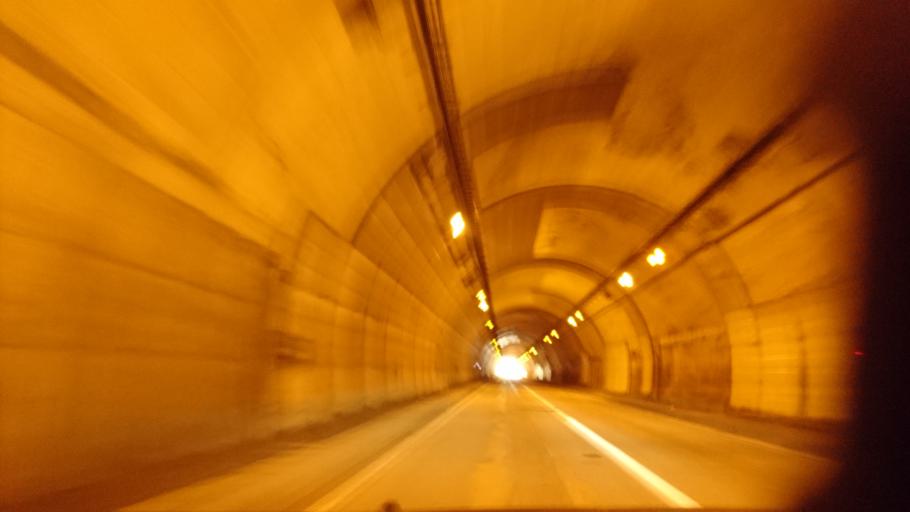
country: JP
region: Iwate
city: Shizukuishi
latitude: 39.6998
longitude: 140.7682
